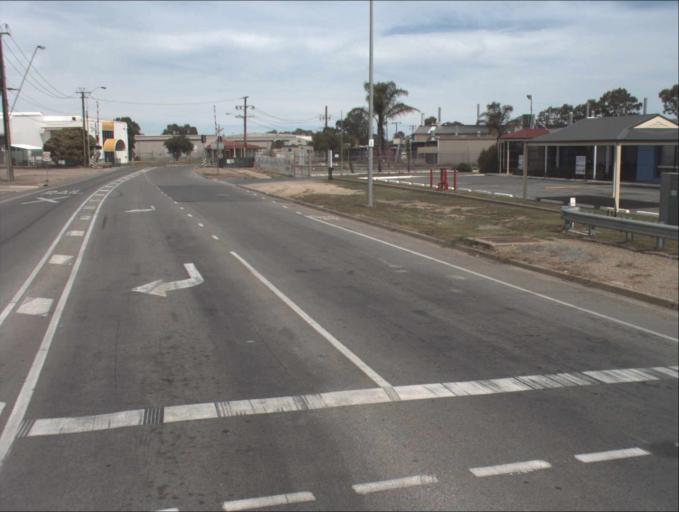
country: AU
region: South Australia
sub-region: Port Adelaide Enfield
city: Alberton
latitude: -34.8405
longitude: 138.5274
